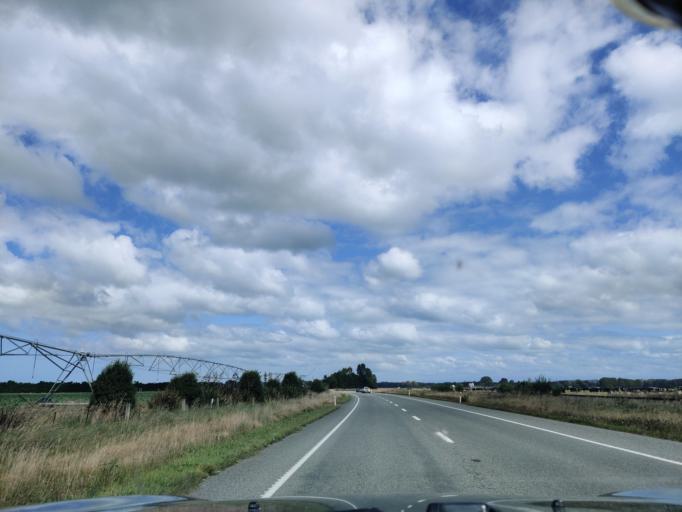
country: NZ
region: Canterbury
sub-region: Timaru District
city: Pleasant Point
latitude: -44.0974
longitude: 171.3210
